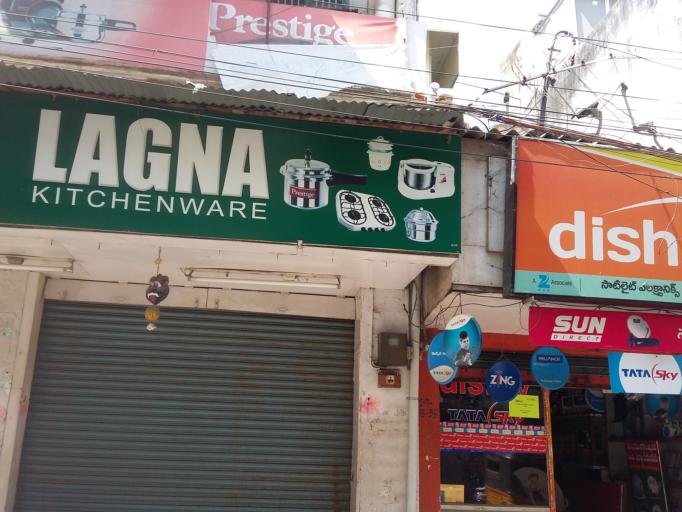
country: IN
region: Andhra Pradesh
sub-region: Chittoor
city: Tirupati
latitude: 13.6330
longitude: 79.4158
